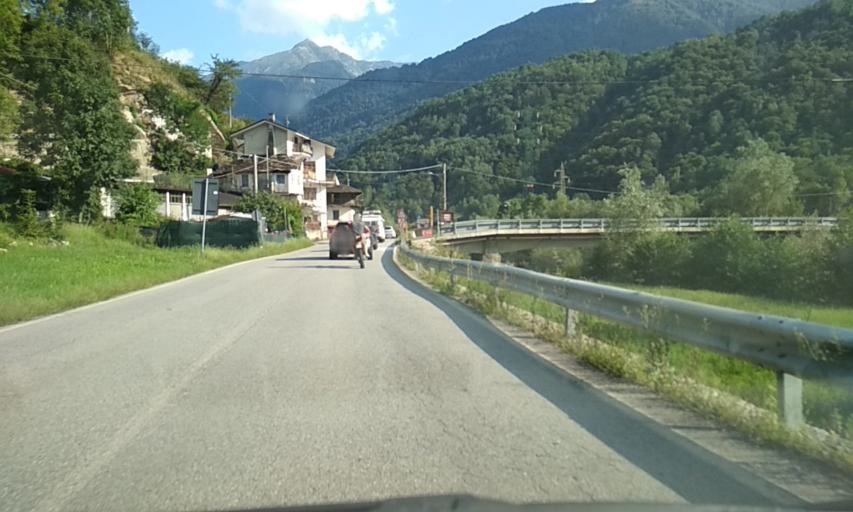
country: IT
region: Piedmont
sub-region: Provincia di Torino
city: Locana
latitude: 45.4217
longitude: 7.4445
